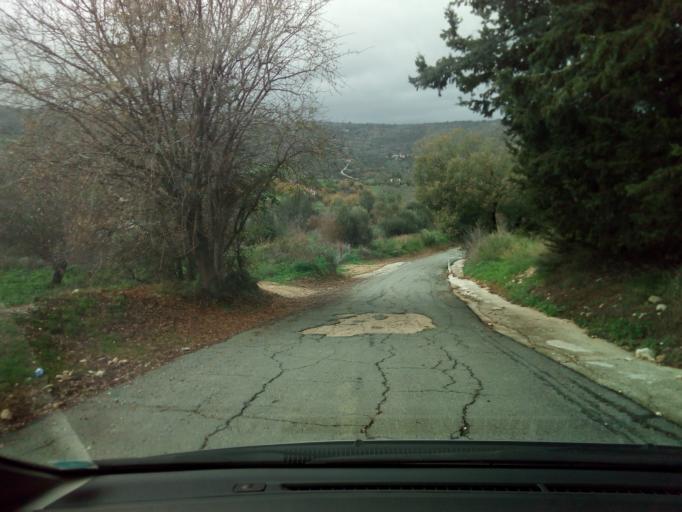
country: CY
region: Pafos
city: Tala
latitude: 34.9284
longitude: 32.4718
